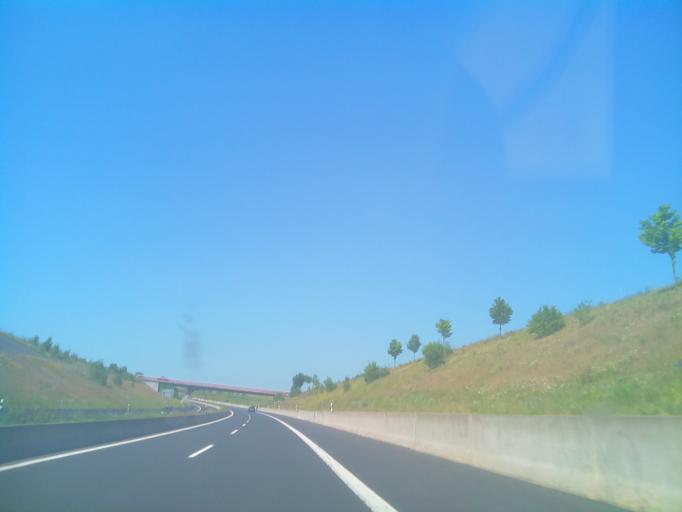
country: DE
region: Bavaria
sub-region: Regierungsbezirk Unterfranken
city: Hollstadt
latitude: 50.3469
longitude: 10.3145
